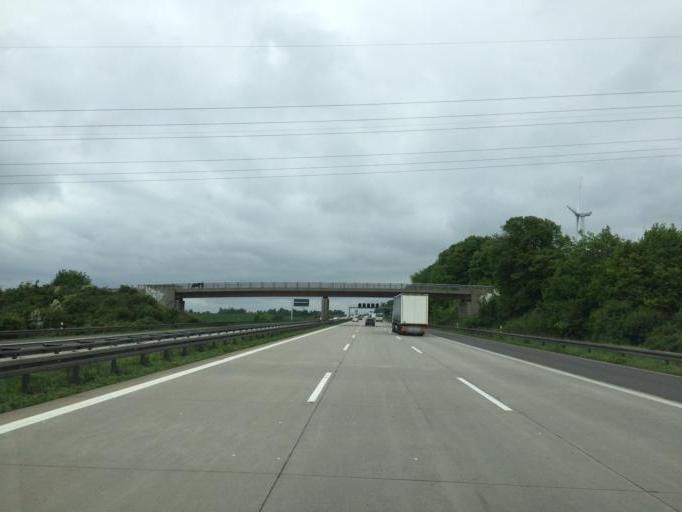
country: DE
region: Saxony-Anhalt
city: Gross Santersleben
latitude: 52.1832
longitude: 11.4557
